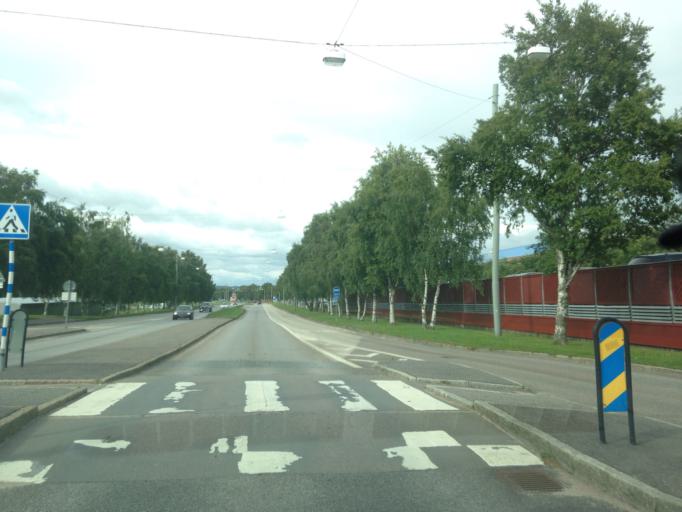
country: SE
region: Vaestra Goetaland
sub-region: Goteborg
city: Goeteborg
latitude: 57.7458
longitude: 11.9774
